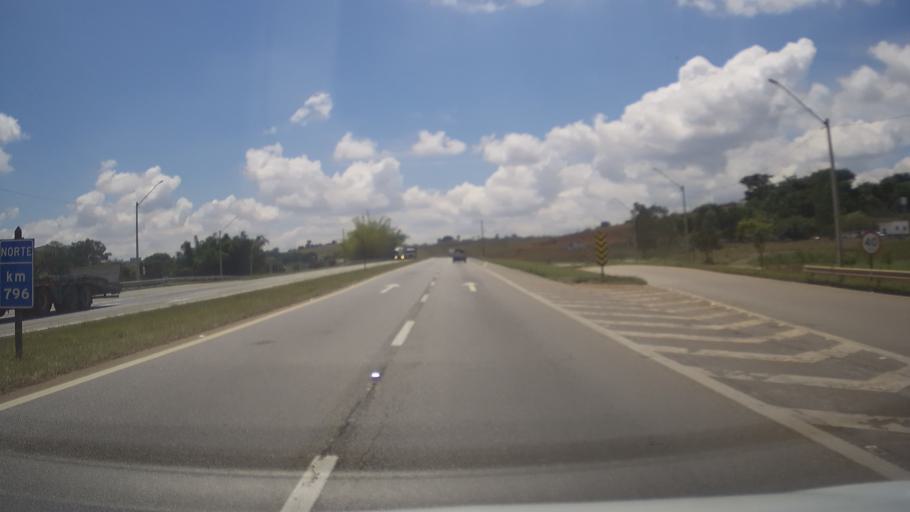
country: BR
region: Minas Gerais
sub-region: Sao Goncalo Do Sapucai
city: Sao Goncalo do Sapucai
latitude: -21.9151
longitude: -45.5812
